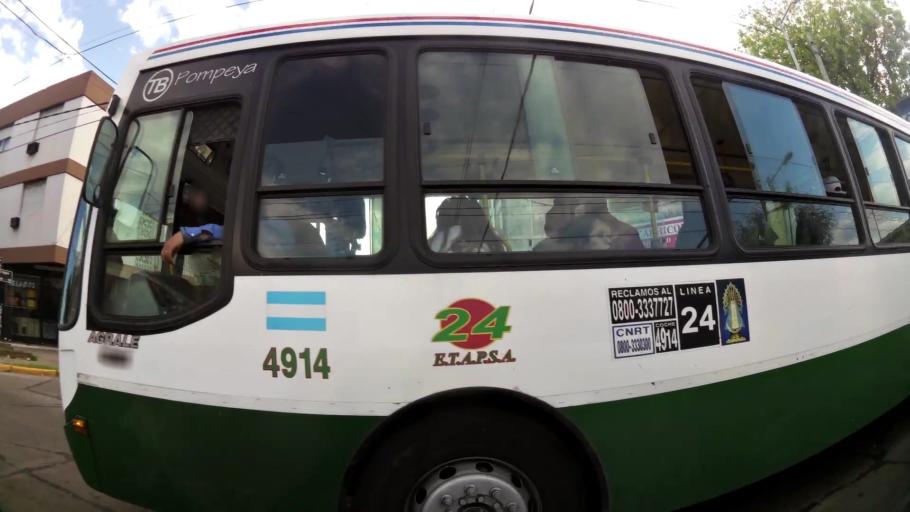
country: AR
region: Buenos Aires
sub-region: Partido de Avellaneda
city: Avellaneda
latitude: -34.6794
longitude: -58.3528
